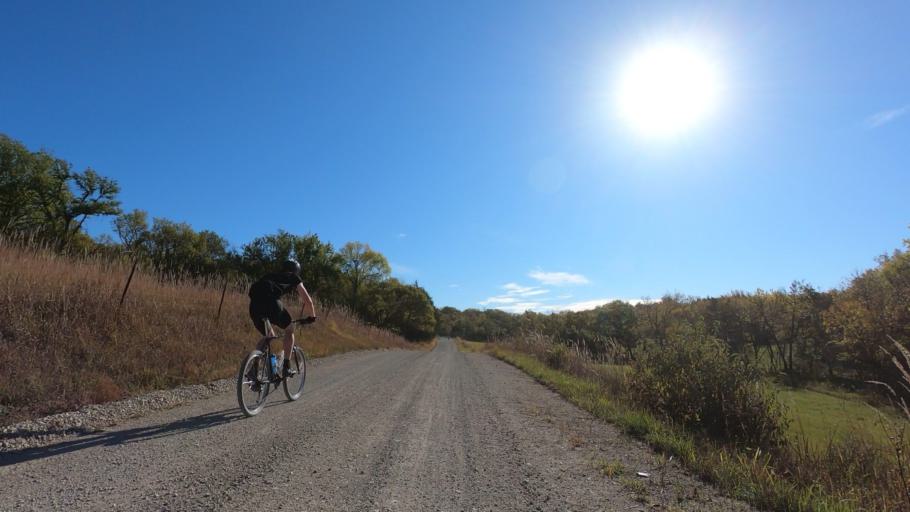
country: US
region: Kansas
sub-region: Pottawatomie County
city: Westmoreland
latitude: 39.4819
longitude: -96.5939
